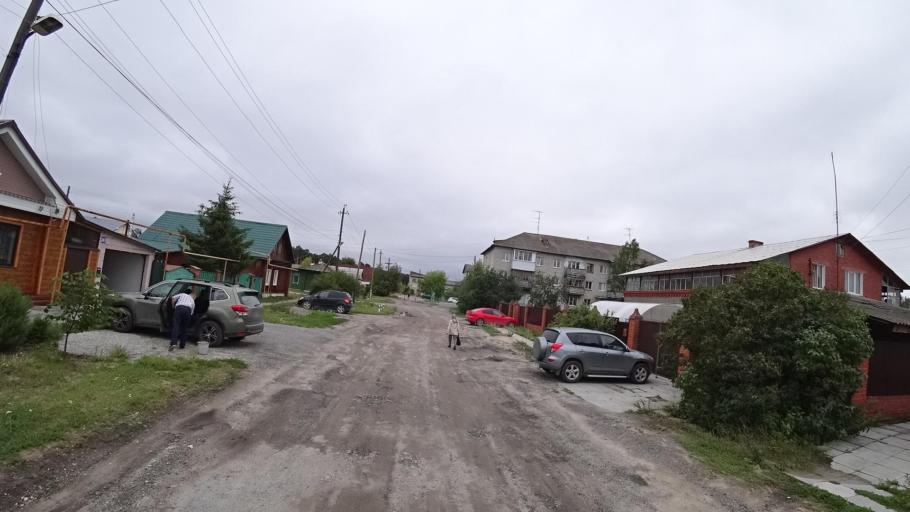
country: RU
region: Sverdlovsk
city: Kamyshlov
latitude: 56.8370
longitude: 62.7195
